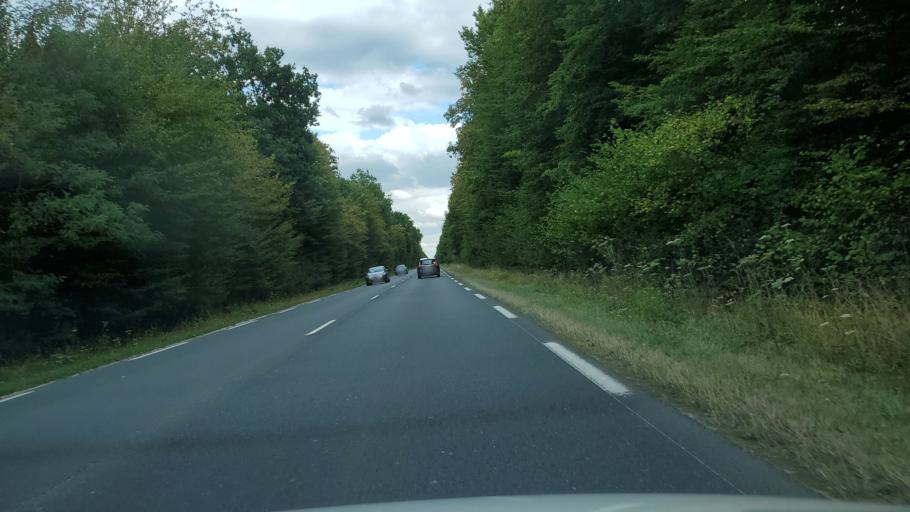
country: FR
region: Ile-de-France
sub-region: Departement de Seine-et-Marne
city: Villeneuve-le-Comte
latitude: 48.8010
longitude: 2.8511
